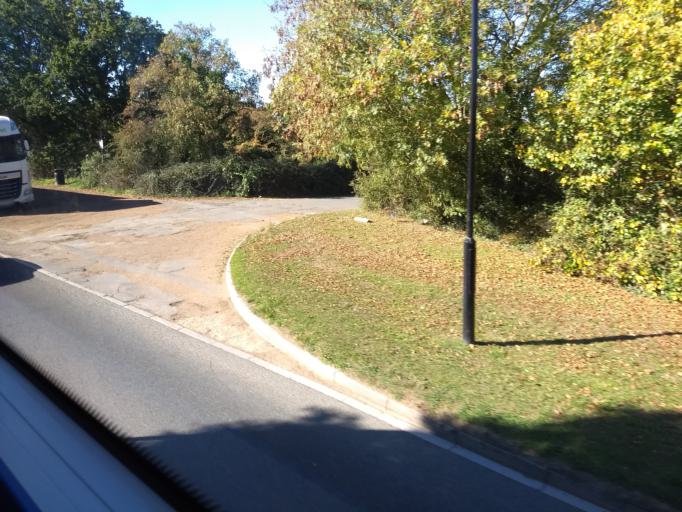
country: GB
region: England
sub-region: Isle of Wight
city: Newport
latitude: 50.7152
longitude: -1.2778
